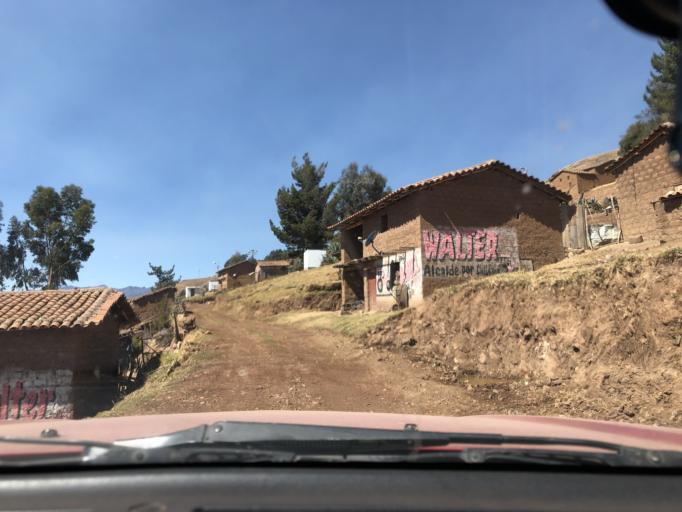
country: PE
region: Ayacucho
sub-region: Provincia de La Mar
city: Chilcas
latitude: -13.1685
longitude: -73.8562
